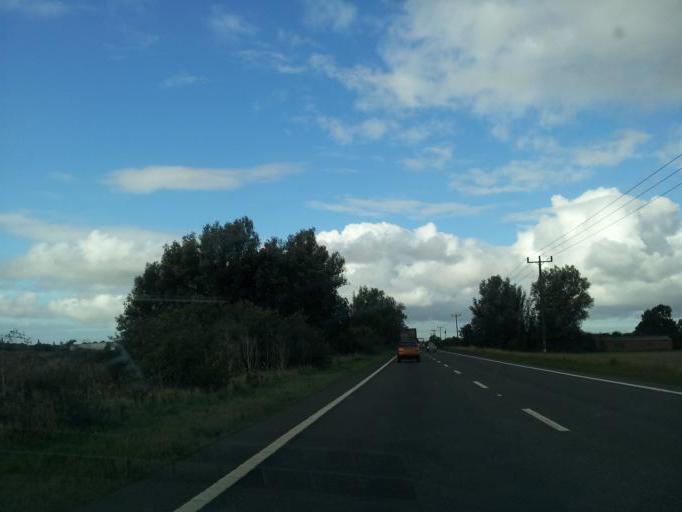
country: GB
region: England
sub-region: Norfolk
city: Clenchwarton
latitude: 52.7471
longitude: 0.3444
